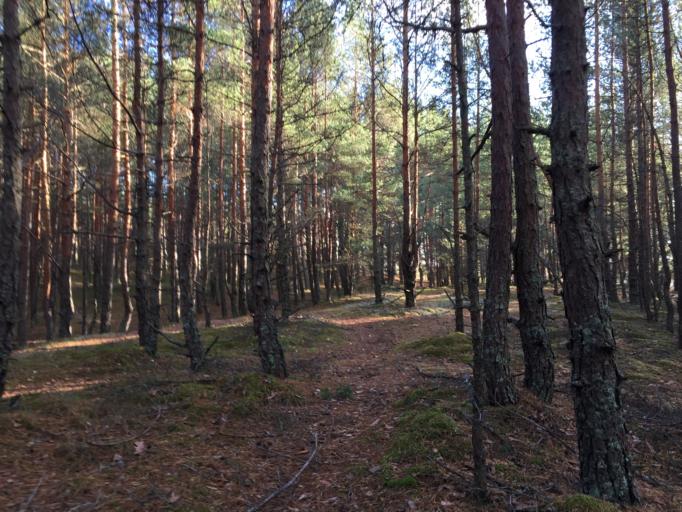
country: LV
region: Carnikava
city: Carnikava
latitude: 57.1550
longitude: 24.2774
